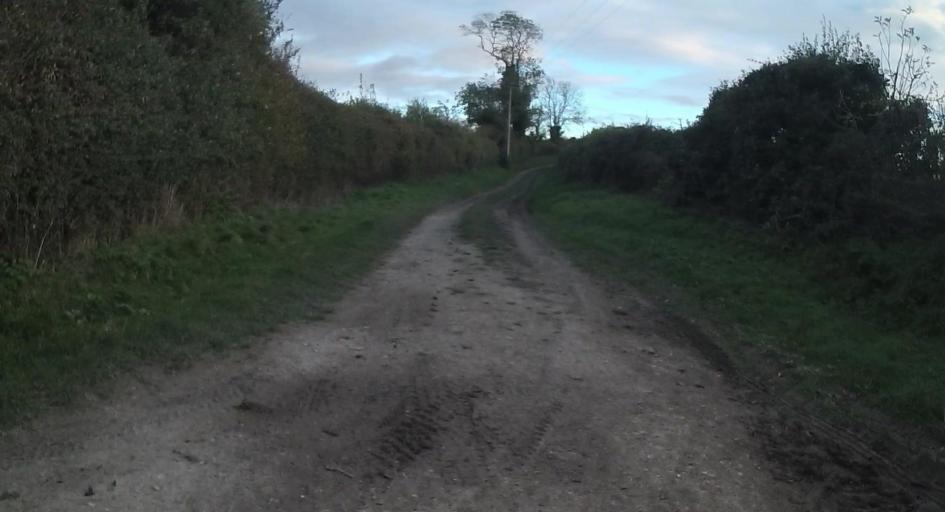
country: GB
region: England
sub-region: Hampshire
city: Andover
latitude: 51.1722
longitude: -1.3903
